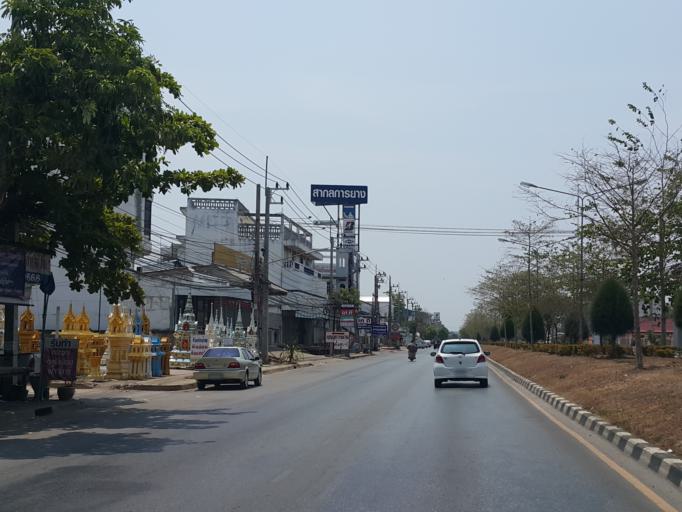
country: TH
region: Kanchanaburi
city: Kanchanaburi
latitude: 14.0424
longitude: 99.5141
